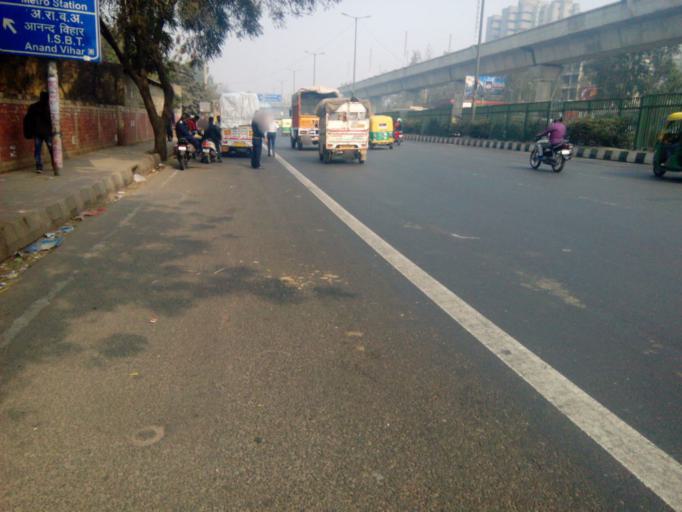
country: IN
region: Uttar Pradesh
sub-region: Gautam Buddha Nagar
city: Noida
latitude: 28.6429
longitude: 77.3162
